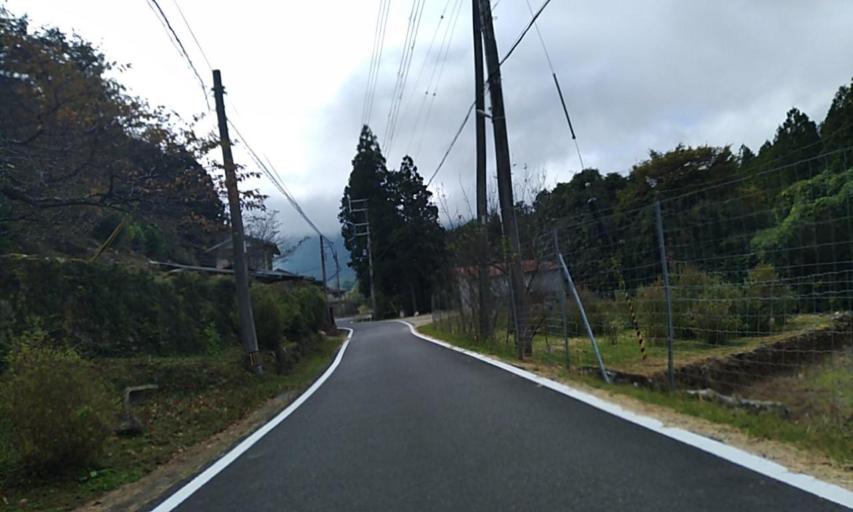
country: JP
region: Wakayama
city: Shingu
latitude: 33.9302
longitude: 135.9794
